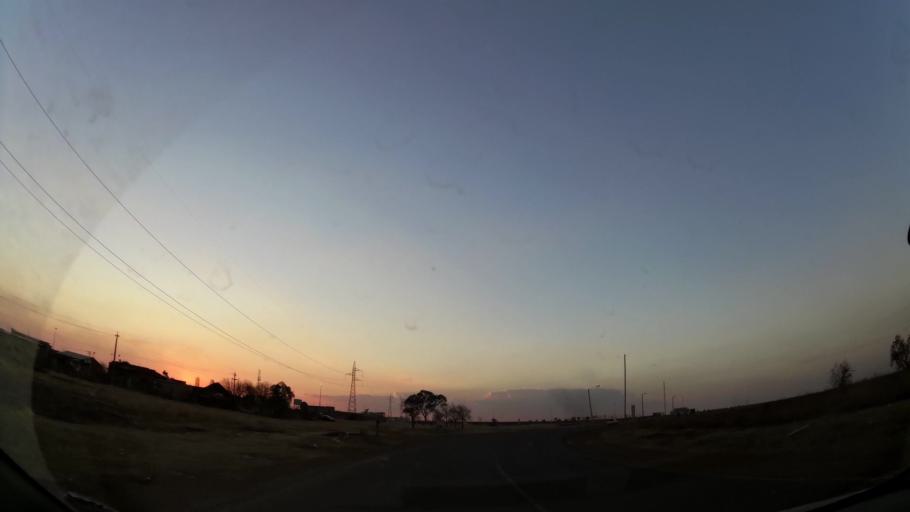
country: ZA
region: Gauteng
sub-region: Ekurhuleni Metropolitan Municipality
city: Nigel
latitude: -26.3787
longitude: 28.4216
